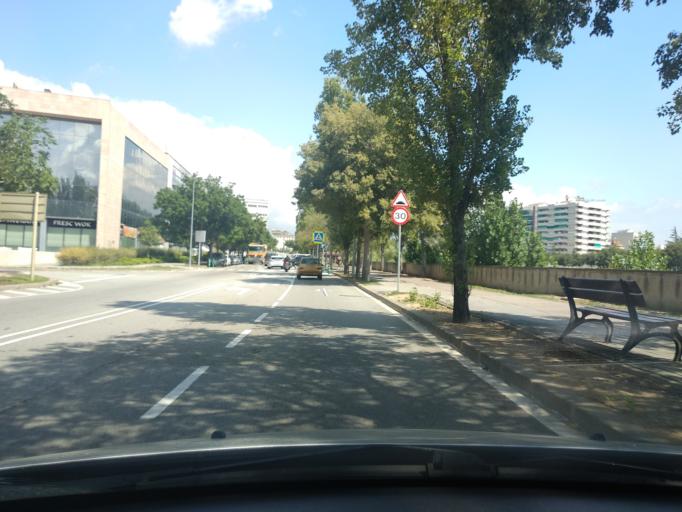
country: ES
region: Catalonia
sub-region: Provincia de Barcelona
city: Granollers
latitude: 41.6084
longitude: 2.2804
